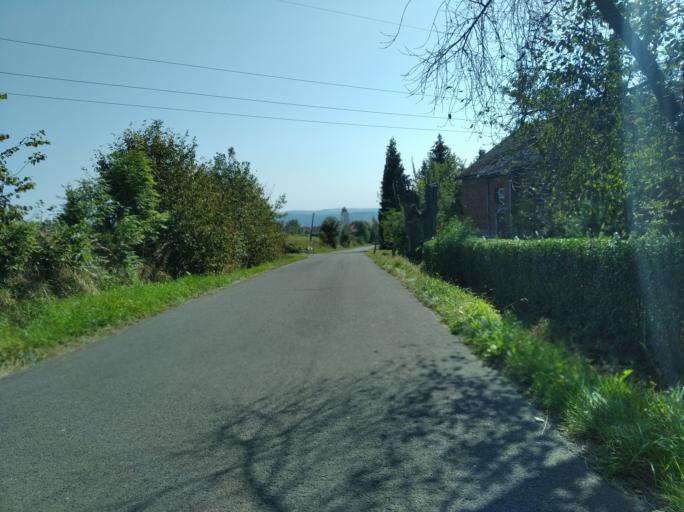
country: PL
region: Subcarpathian Voivodeship
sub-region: Powiat strzyzowski
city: Czudec
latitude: 49.9603
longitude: 21.8279
